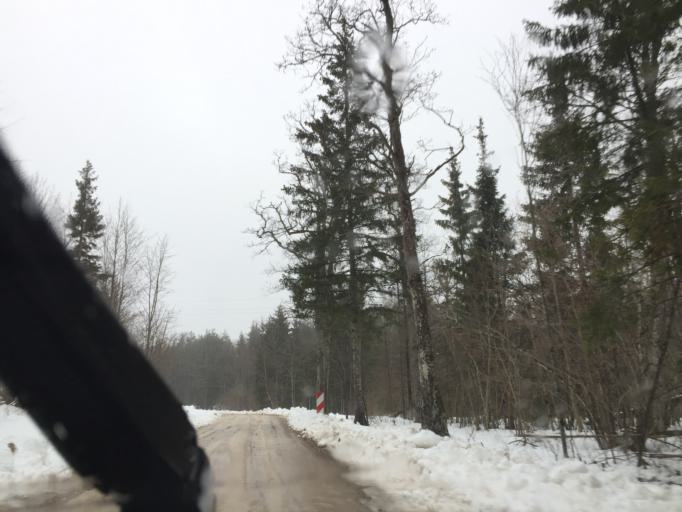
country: EE
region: Saare
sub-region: Kuressaare linn
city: Kuressaare
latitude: 58.2935
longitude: 22.1050
